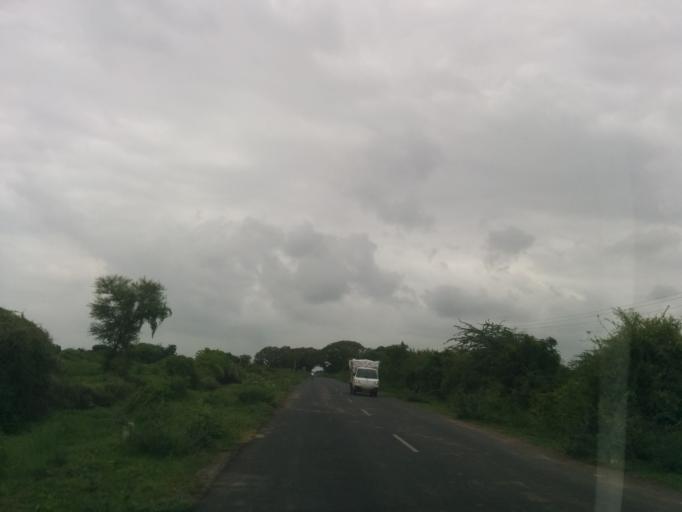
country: IN
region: Gujarat
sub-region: Ahmadabad
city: Sanand
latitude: 23.0809
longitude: 72.4075
